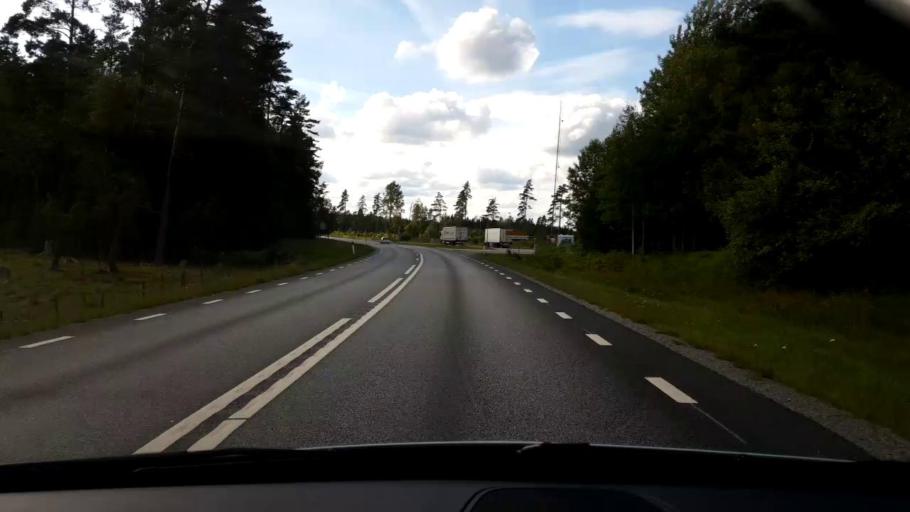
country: SE
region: Joenkoeping
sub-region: Savsjo Kommun
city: Vrigstad
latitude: 57.3654
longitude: 14.4511
